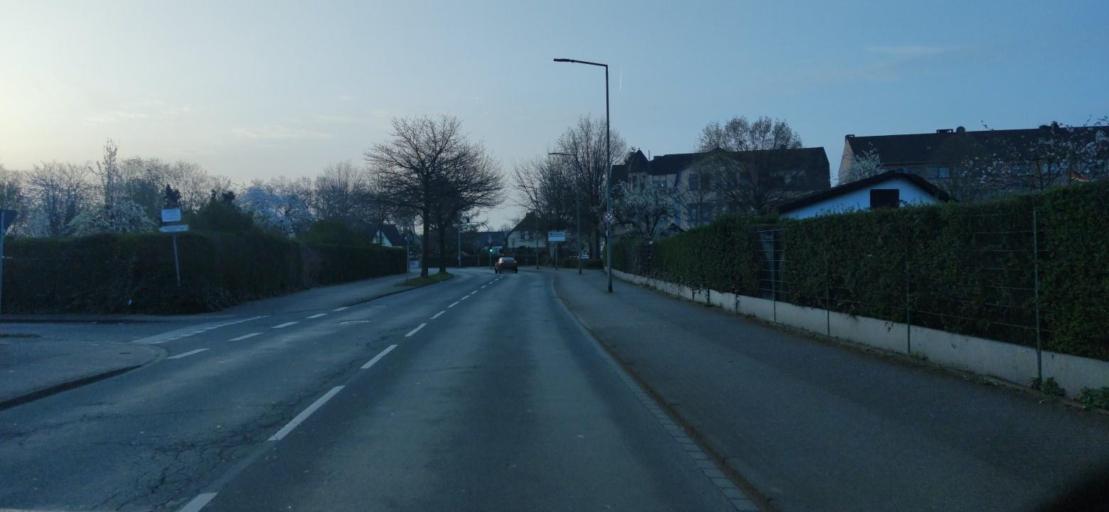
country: DE
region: North Rhine-Westphalia
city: Meiderich
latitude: 51.4981
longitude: 6.7862
